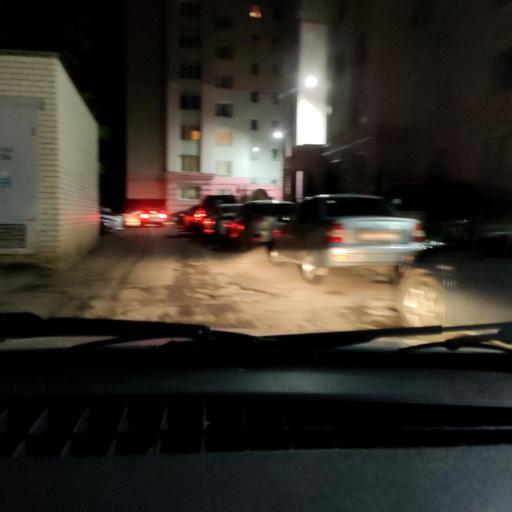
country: RU
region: Voronezj
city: Voronezh
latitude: 51.7158
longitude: 39.2201
